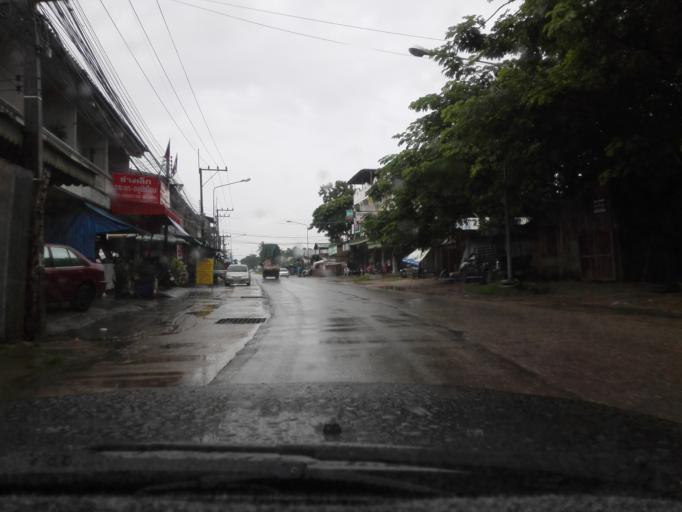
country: TH
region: Tak
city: Mae Sot
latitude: 16.7073
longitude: 98.5712
